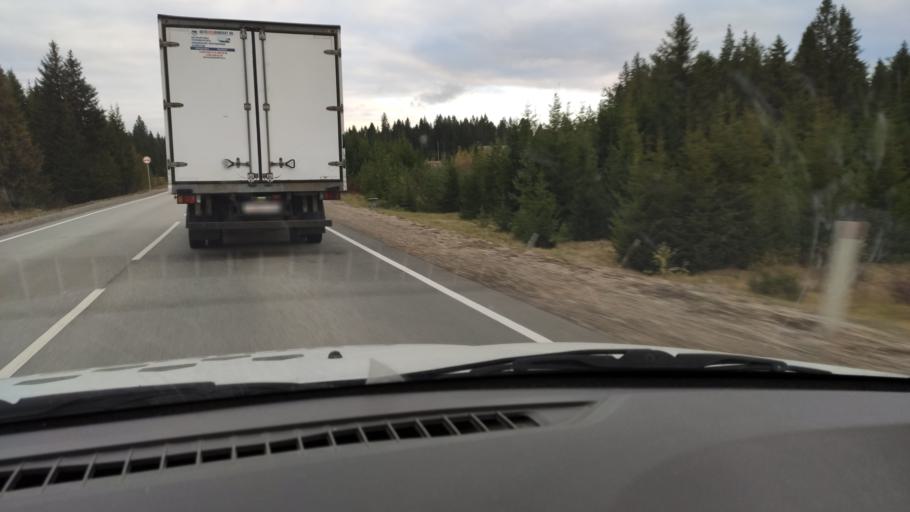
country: RU
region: Kirov
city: Chernaya Kholunitsa
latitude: 58.8541
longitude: 51.7312
